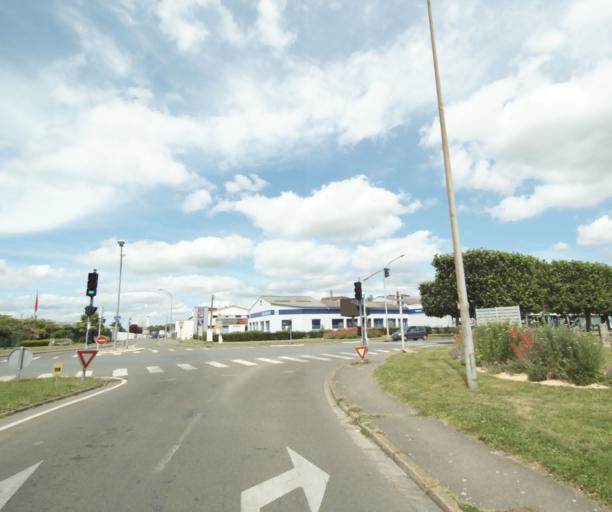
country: FR
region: Centre
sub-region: Departement d'Eure-et-Loir
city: Luce
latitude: 48.4309
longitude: 1.4641
